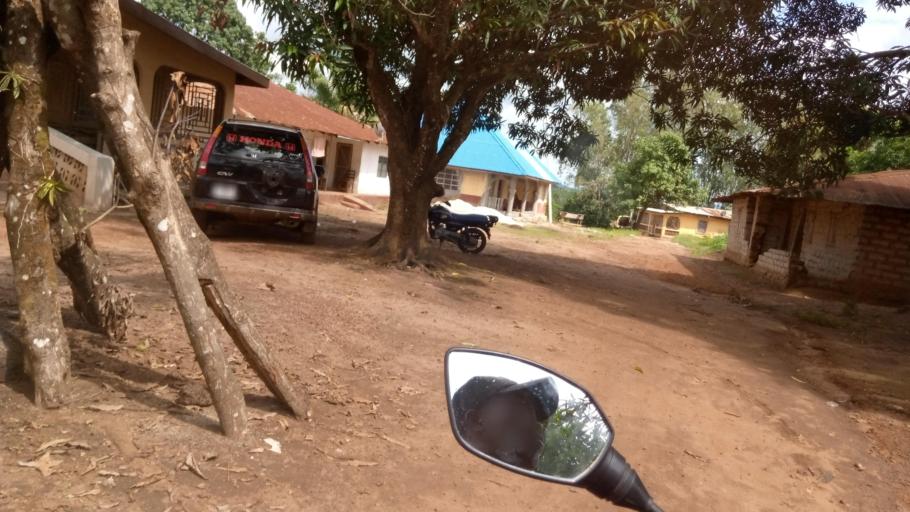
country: SL
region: Northern Province
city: Kamakwie
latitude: 9.4924
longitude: -12.2340
